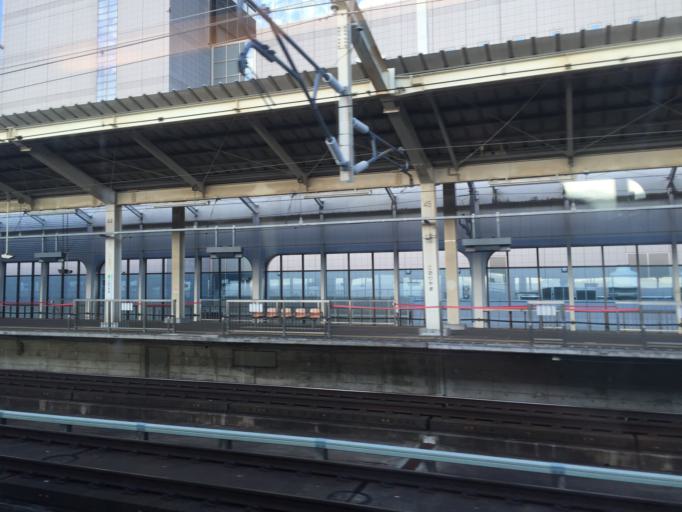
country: JP
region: Fukushima
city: Koriyama
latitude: 37.3999
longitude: 140.3890
